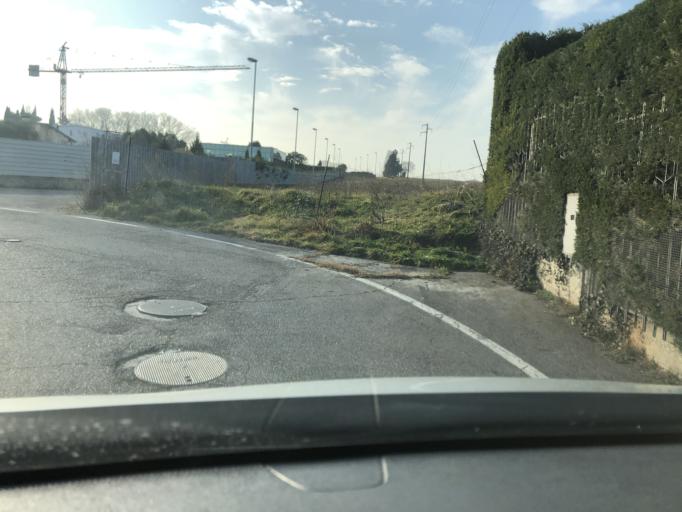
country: IT
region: Veneto
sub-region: Provincia di Verona
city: Sommacampagna
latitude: 45.4149
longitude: 10.8472
